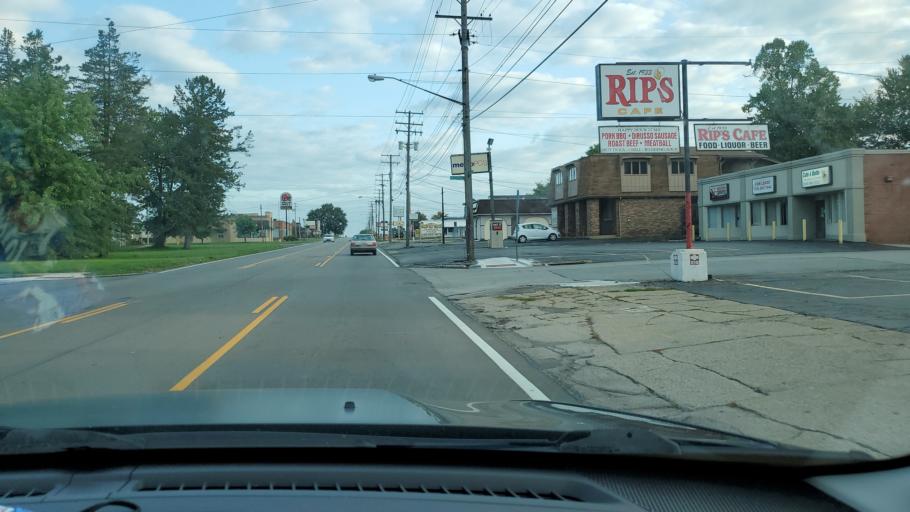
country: US
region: Ohio
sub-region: Mahoning County
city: Struthers
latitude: 41.0546
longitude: -80.6158
